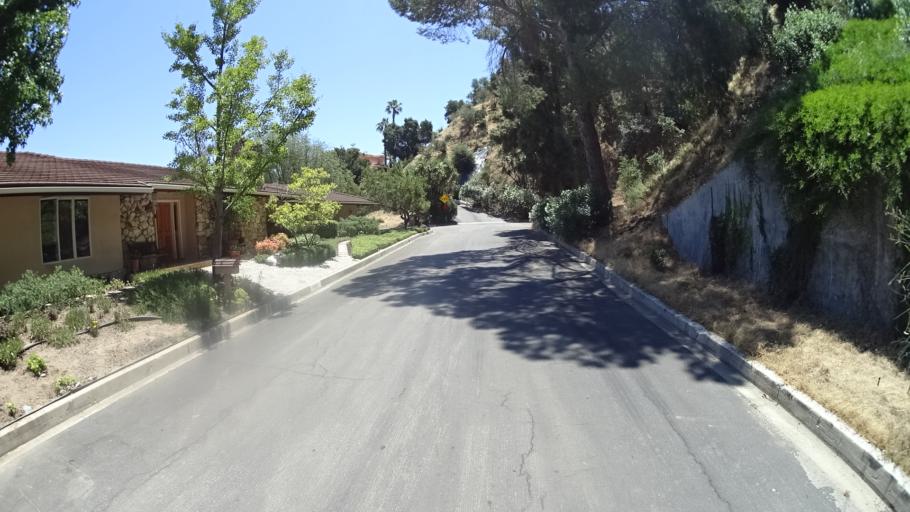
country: US
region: California
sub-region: Los Angeles County
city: Universal City
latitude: 34.1337
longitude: -118.3727
